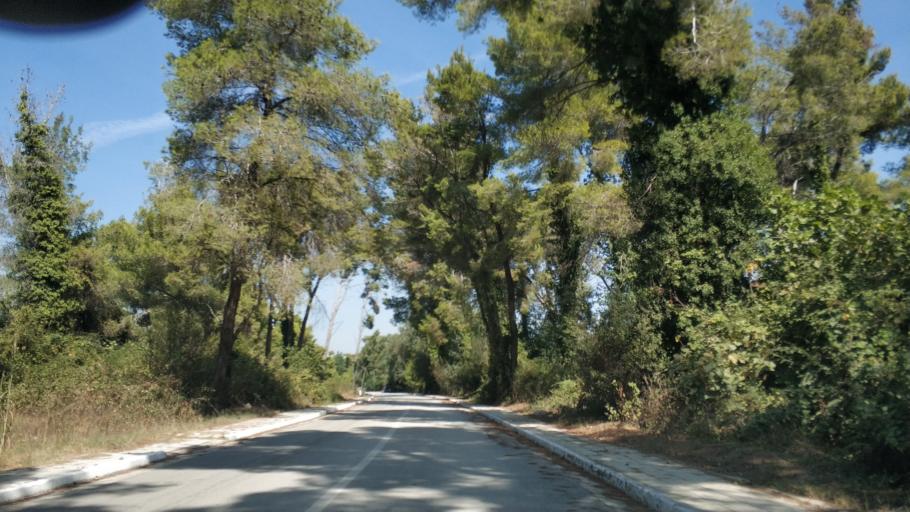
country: AL
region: Fier
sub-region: Rrethi i Lushnjes
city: Divjake
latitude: 40.9647
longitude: 19.4777
